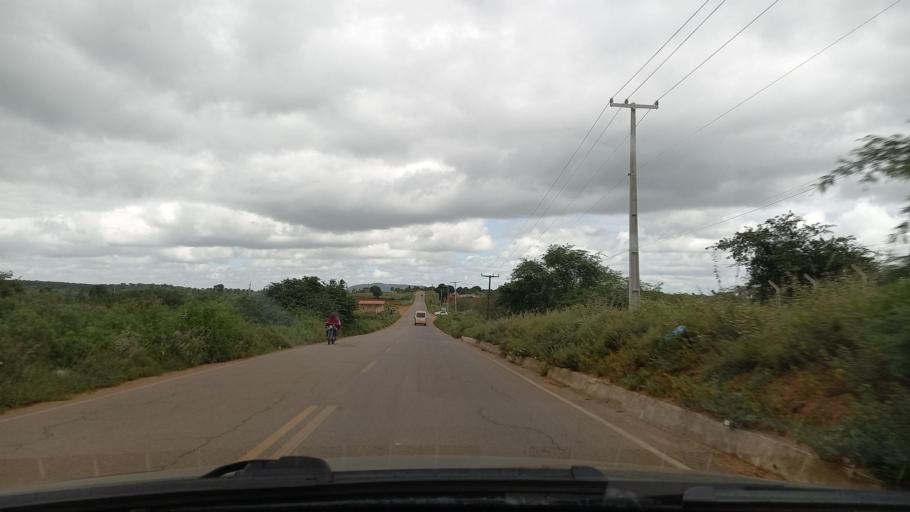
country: BR
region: Sergipe
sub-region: Caninde De Sao Francisco
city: Caninde de Sao Francisco
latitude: -9.6721
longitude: -37.7996
